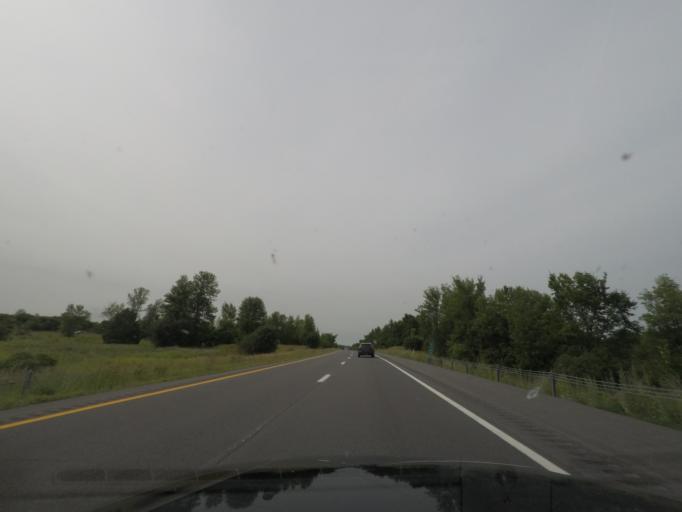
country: US
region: New York
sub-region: Clinton County
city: Cumberland Head
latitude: 44.7520
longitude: -73.4275
